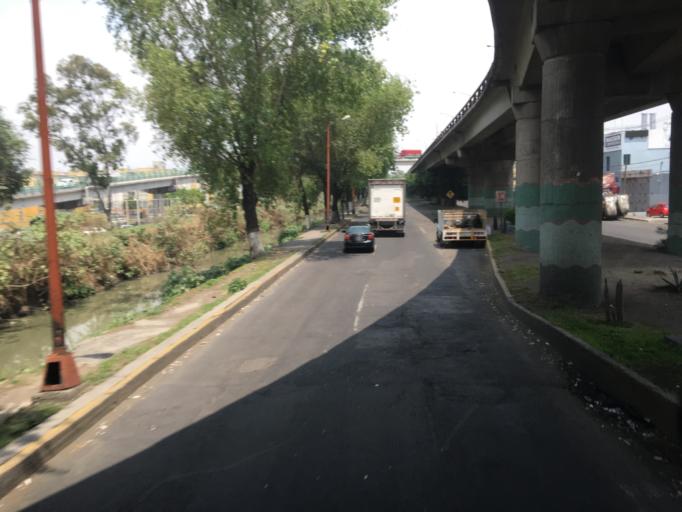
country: MX
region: Mexico
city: Tlalnepantla
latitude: 19.5303
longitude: -99.1703
